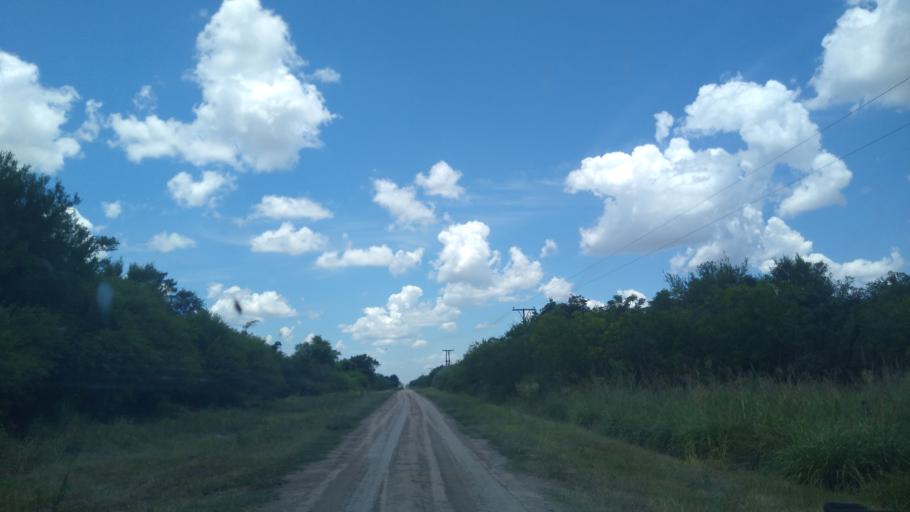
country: AR
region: Chaco
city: Presidencia Roque Saenz Pena
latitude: -26.7469
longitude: -60.3360
